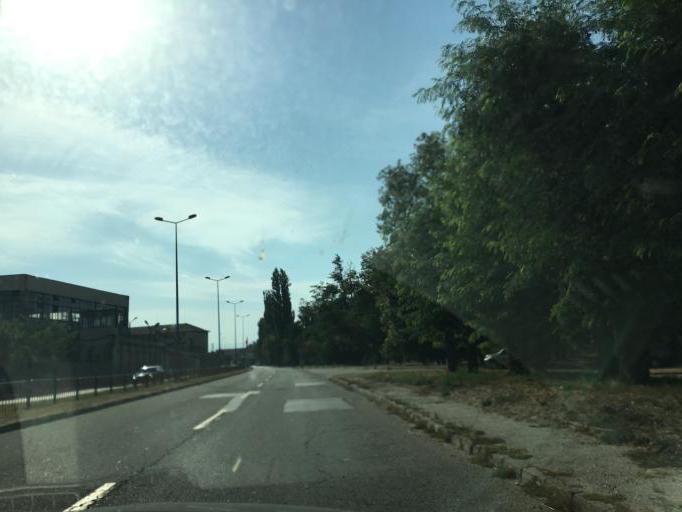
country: BG
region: Pazardzhik
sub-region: Obshtina Pazardzhik
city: Pazardzhik
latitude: 42.2111
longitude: 24.3237
